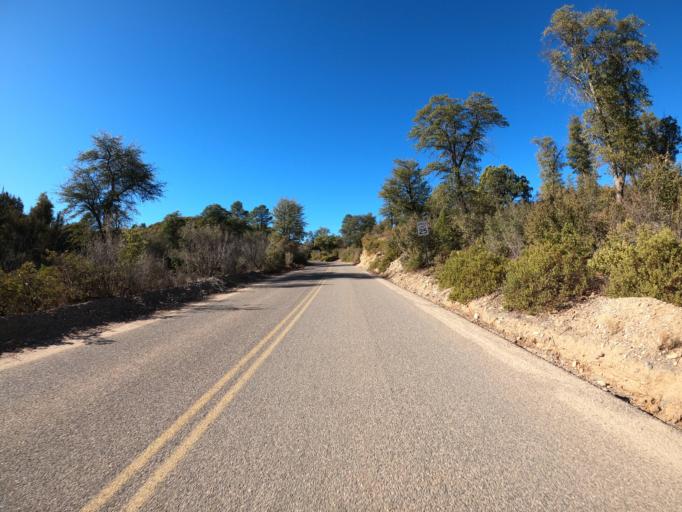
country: US
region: Arizona
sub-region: Yavapai County
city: Verde Village
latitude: 34.5883
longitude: -112.0541
